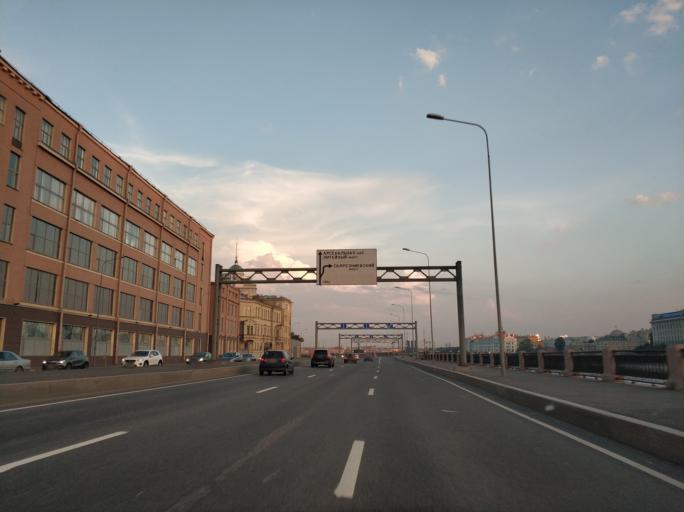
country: RU
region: Leningrad
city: Sampsonievskiy
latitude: 59.9622
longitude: 30.3379
